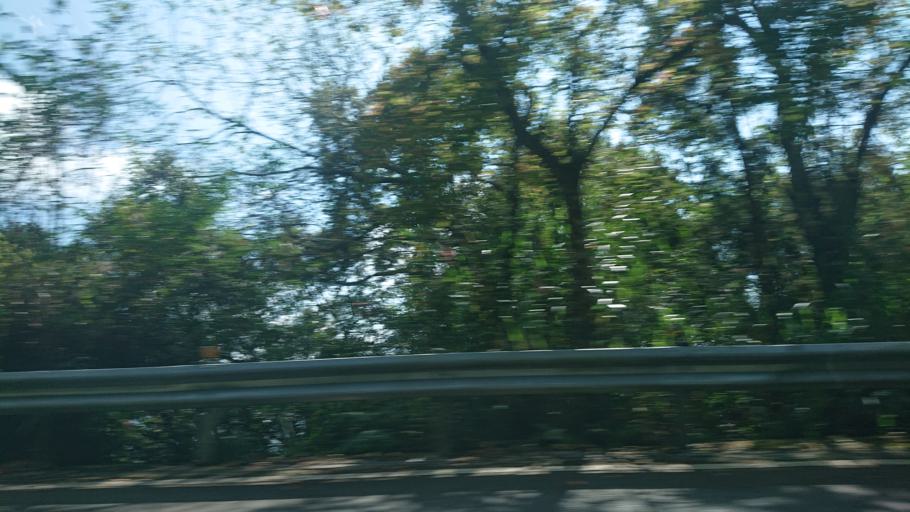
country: TW
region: Taiwan
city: Lugu
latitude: 23.5030
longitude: 120.7975
